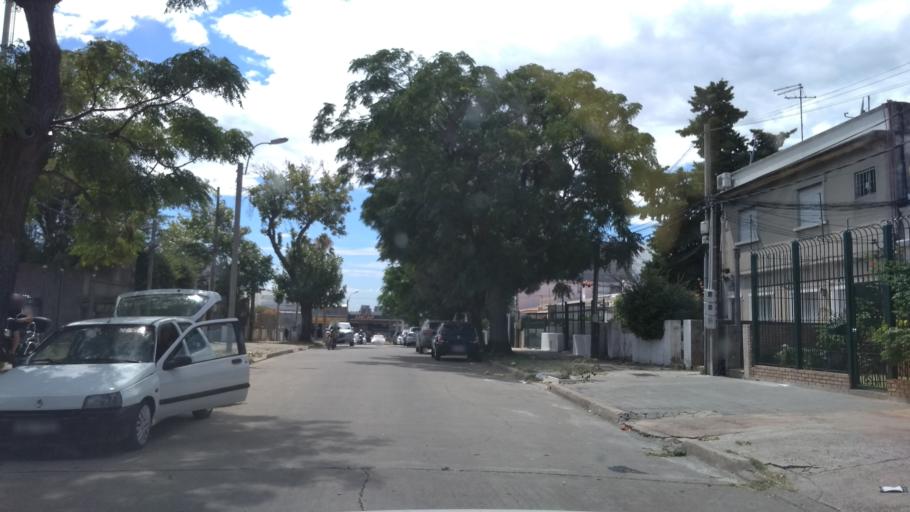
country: UY
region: Montevideo
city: Montevideo
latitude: -34.8882
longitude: -56.1232
